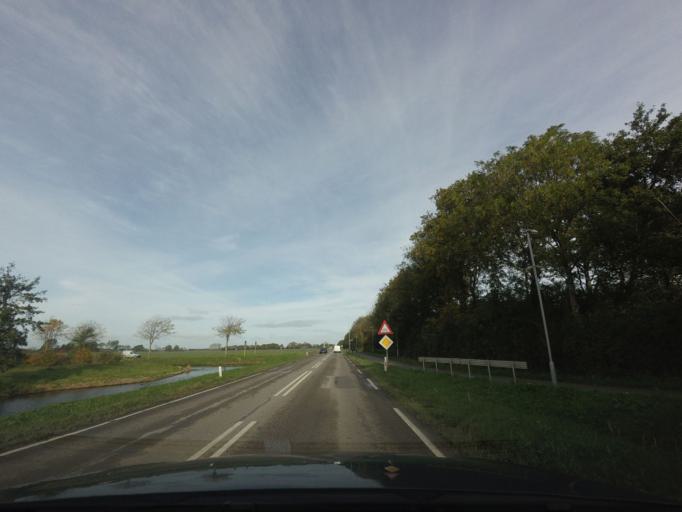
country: NL
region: North Holland
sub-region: Gemeente Schagen
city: Harenkarspel
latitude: 52.7118
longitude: 4.7966
